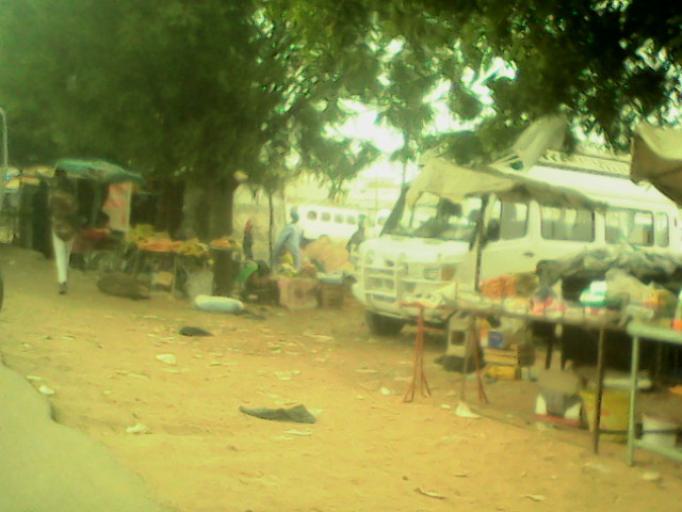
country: SN
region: Diourbel
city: Touba
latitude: 14.8808
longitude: -15.8932
